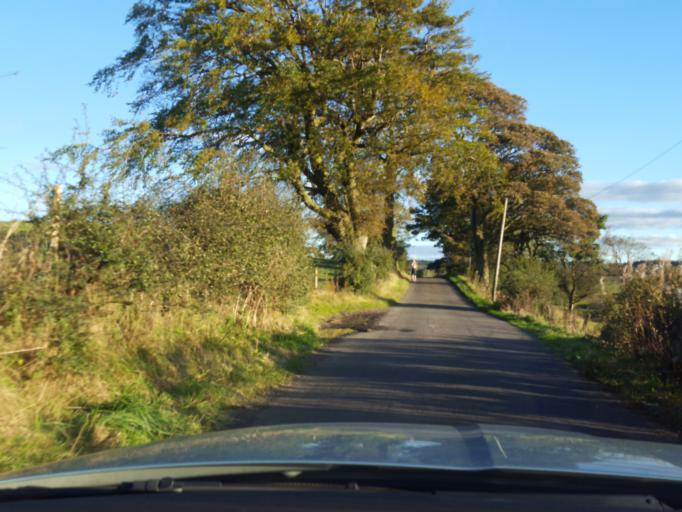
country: GB
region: Scotland
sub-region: North Lanarkshire
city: Cumbernauld
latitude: 55.9265
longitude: -3.9397
